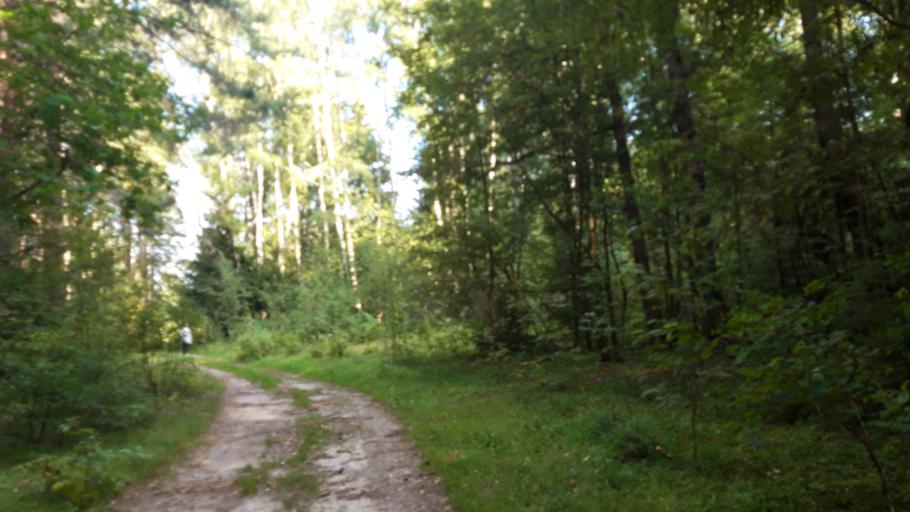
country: RU
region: Tverskaya
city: Konakovo
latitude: 56.6902
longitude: 36.7200
